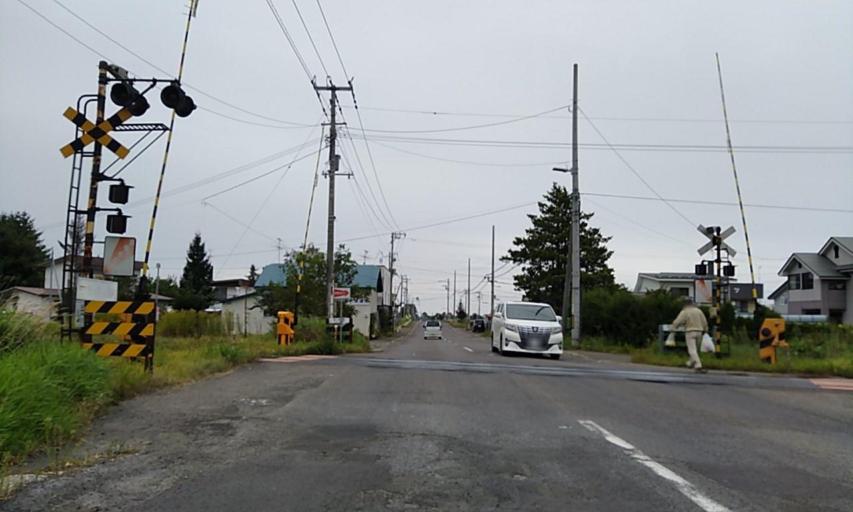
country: JP
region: Hokkaido
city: Bihoro
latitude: 43.8339
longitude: 144.1093
